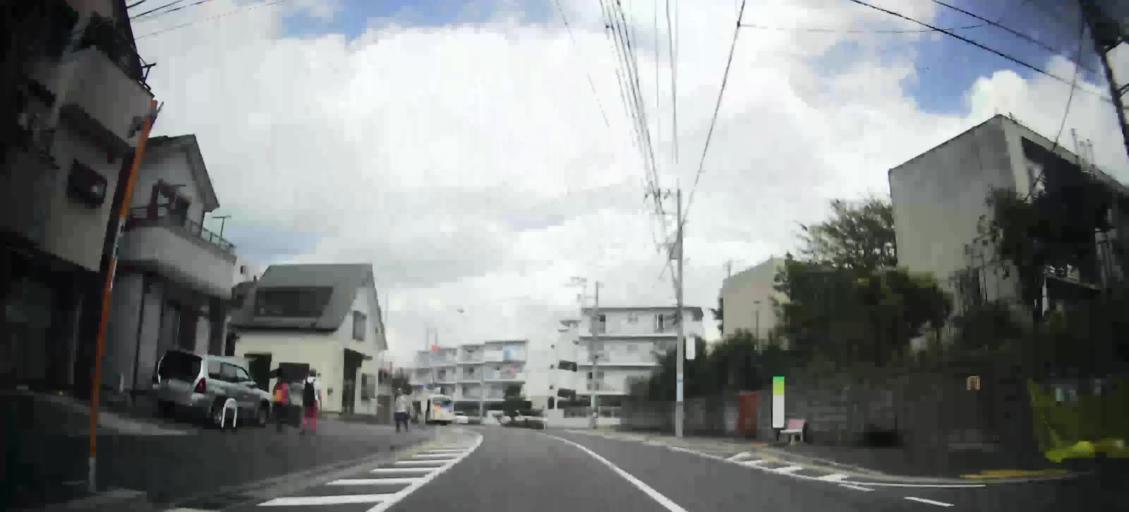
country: JP
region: Kanagawa
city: Minami-rinkan
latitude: 35.4795
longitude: 139.5486
